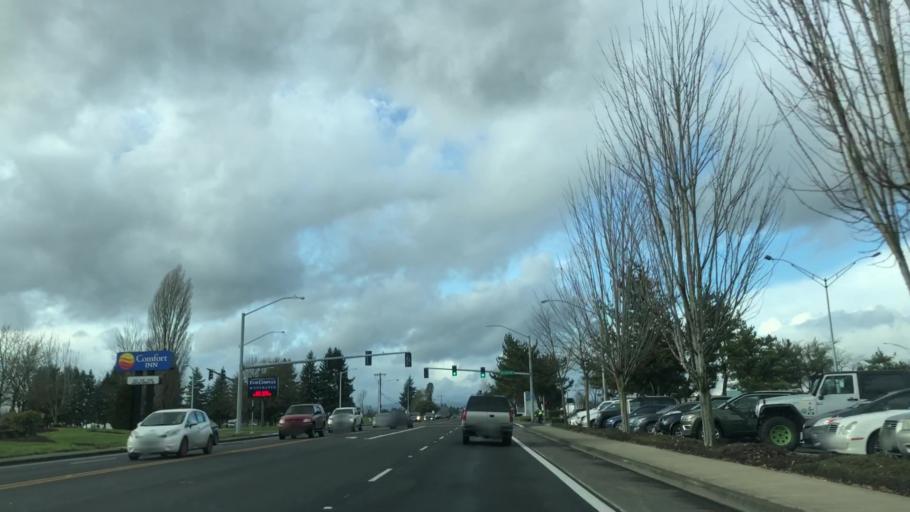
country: US
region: Oregon
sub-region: Washington County
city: Hillsboro
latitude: 45.5323
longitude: -122.9455
